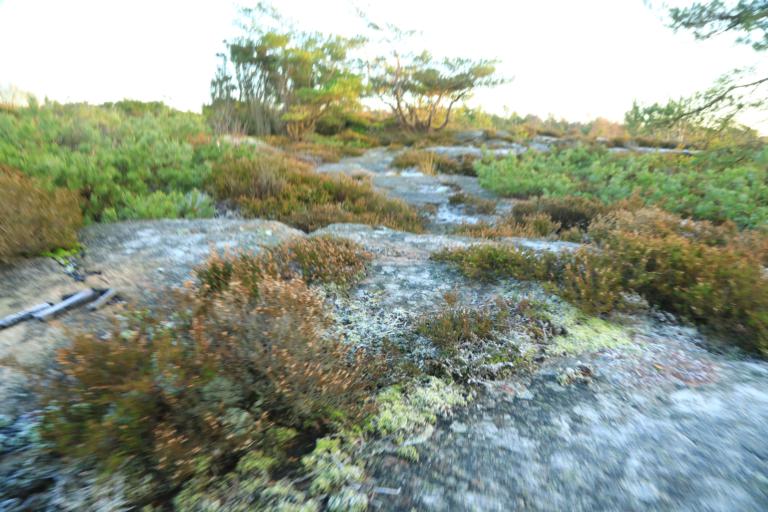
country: SE
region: Halland
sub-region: Kungsbacka Kommun
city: Frillesas
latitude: 57.1963
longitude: 12.1635
